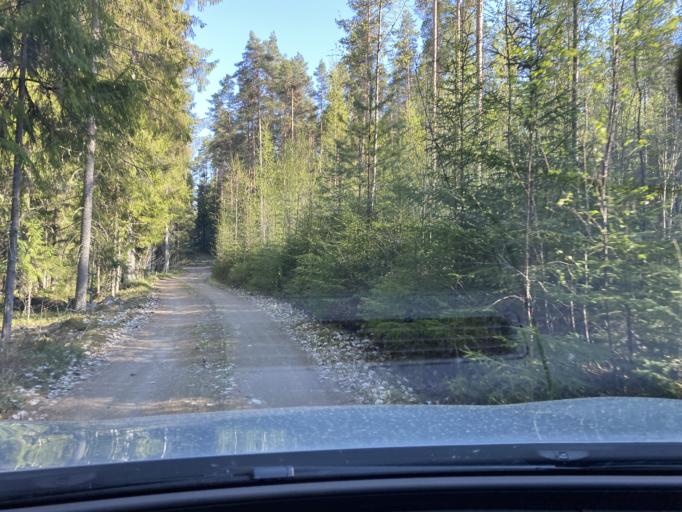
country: FI
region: Pirkanmaa
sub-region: Lounais-Pirkanmaa
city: Punkalaidun
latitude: 61.0159
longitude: 23.1999
